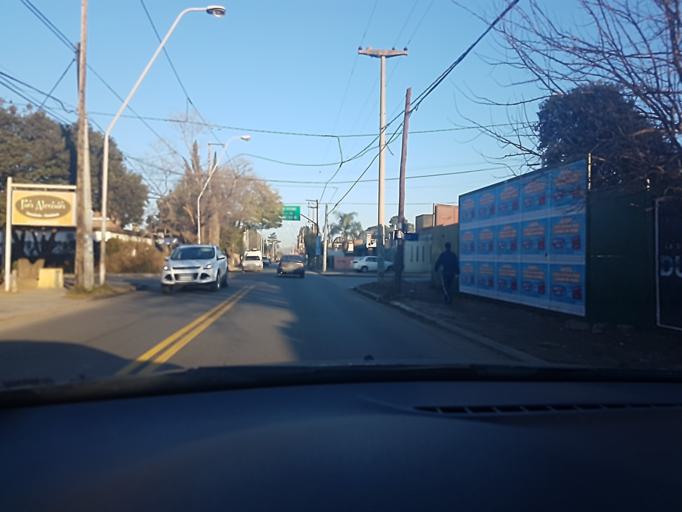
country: AR
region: Cordoba
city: Villa Allende
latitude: -31.3433
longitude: -64.2336
